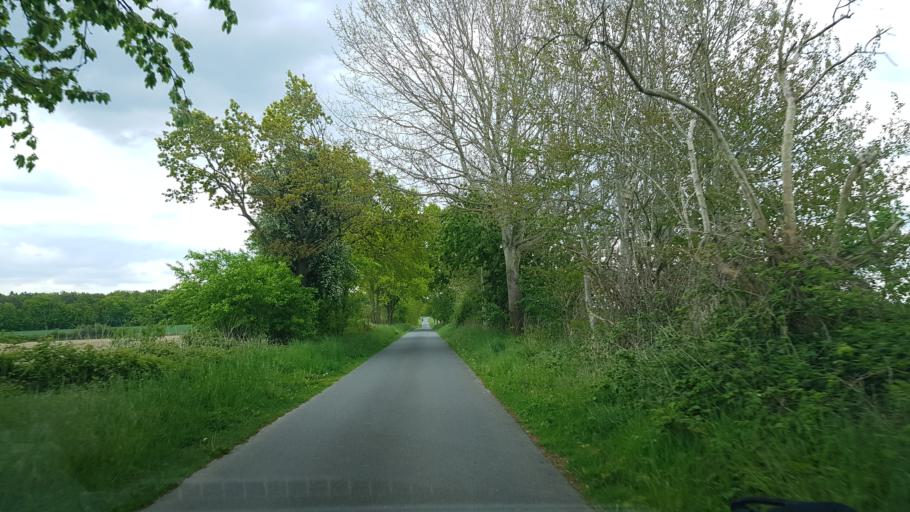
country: DE
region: Lower Saxony
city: Vastorf
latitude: 53.1930
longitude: 10.5555
